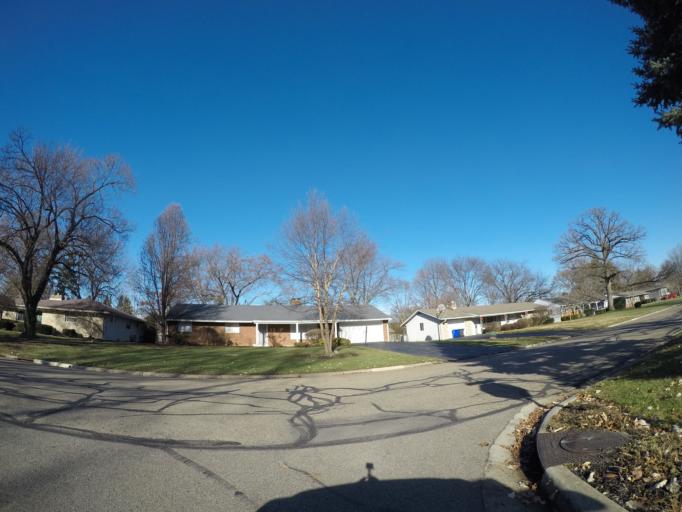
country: US
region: Ohio
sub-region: Franklin County
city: Upper Arlington
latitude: 40.0230
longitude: -83.0511
